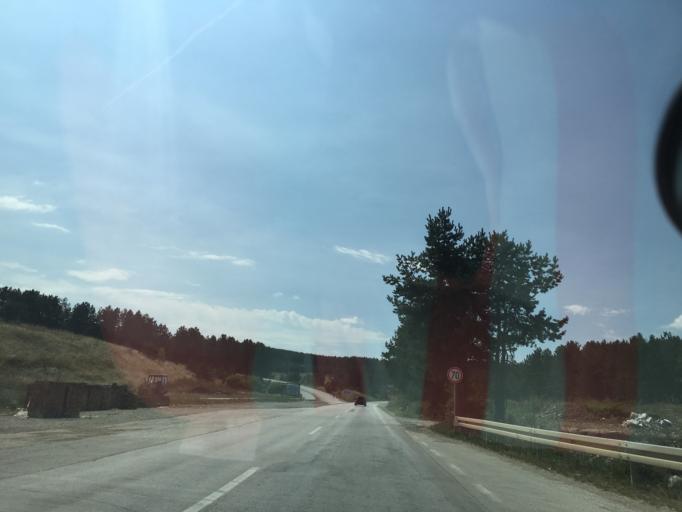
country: RS
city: Zlatibor
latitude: 43.7236
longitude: 19.7063
